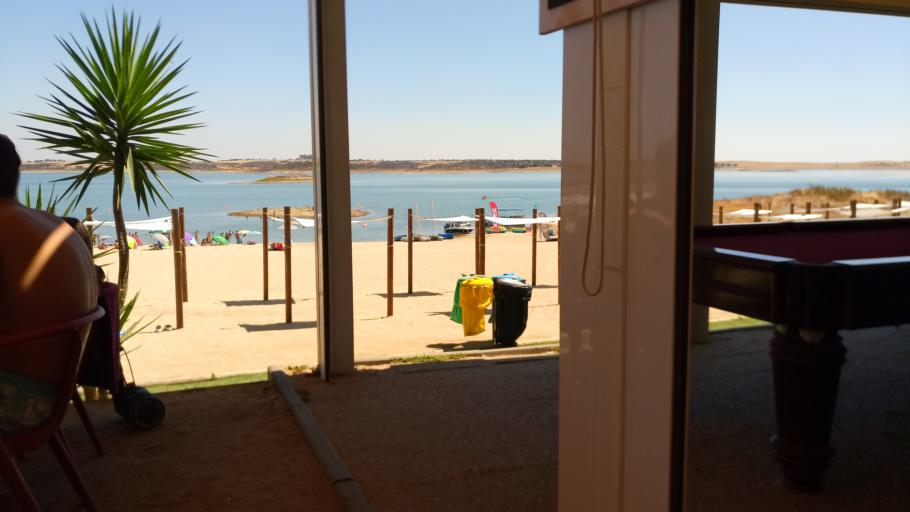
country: PT
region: Evora
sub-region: Mourao
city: Mourao
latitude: 38.4342
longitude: -7.3507
